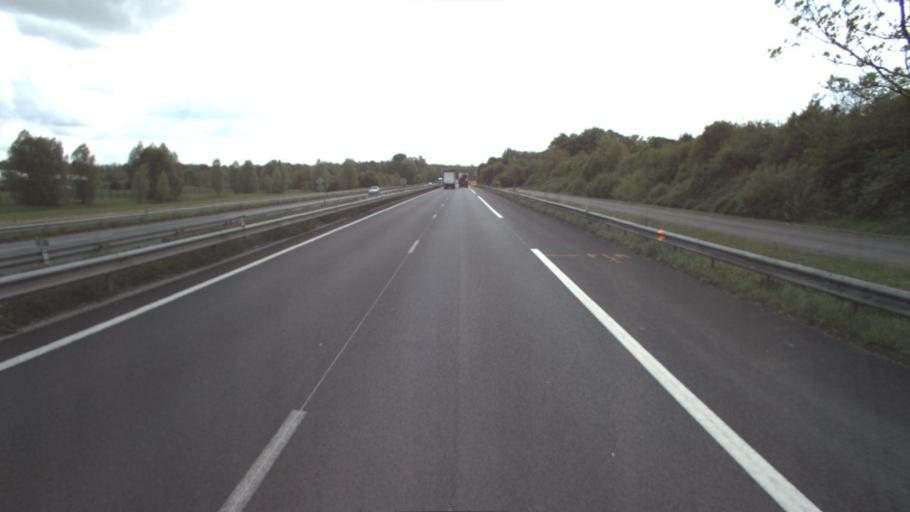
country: FR
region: Ile-de-France
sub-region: Departement de Seine-et-Marne
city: Fontenay-Tresigny
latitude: 48.7215
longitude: 2.8384
